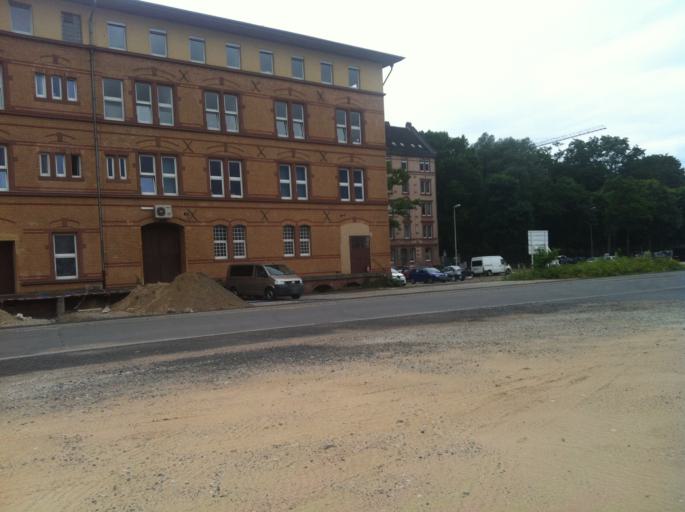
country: DE
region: Rheinland-Pfalz
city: Mainz
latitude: 50.0049
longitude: 8.2537
